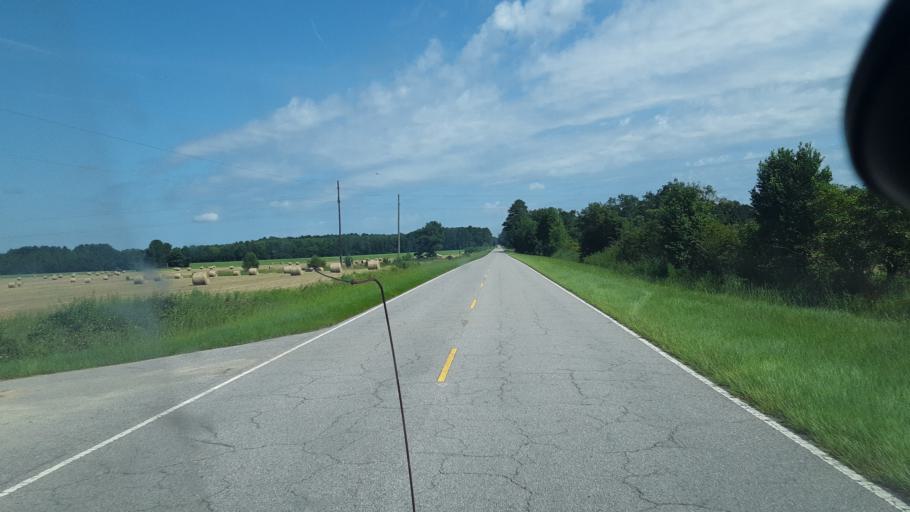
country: US
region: South Carolina
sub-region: Hampton County
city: Hampton
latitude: 33.0447
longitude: -81.0324
